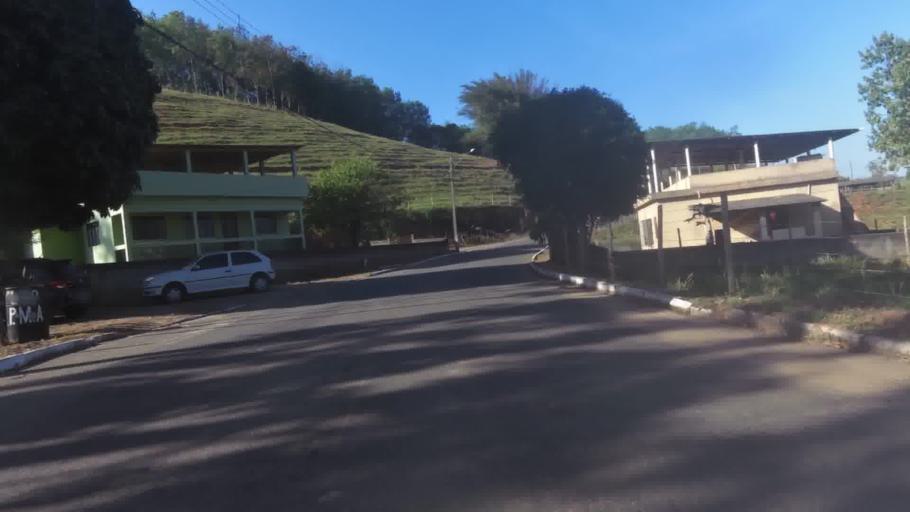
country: BR
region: Espirito Santo
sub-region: Iconha
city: Iconha
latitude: -20.7338
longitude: -40.7827
